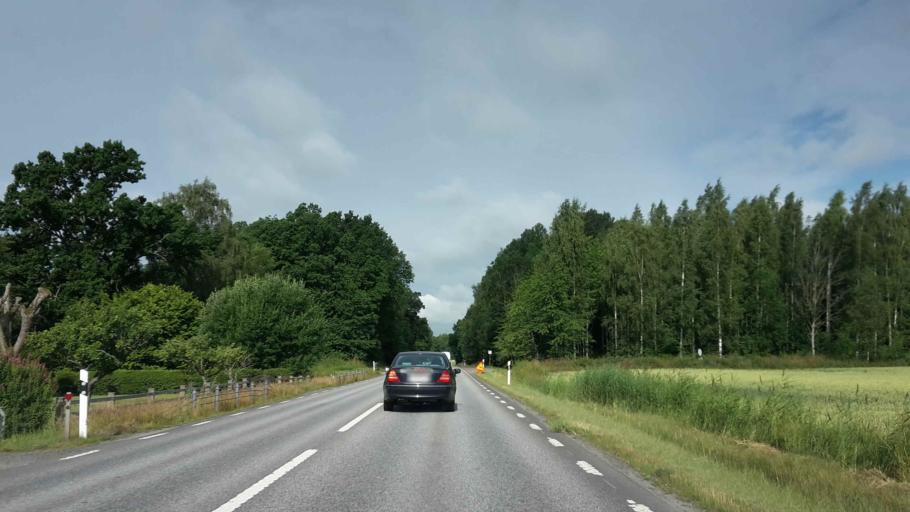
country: SE
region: OEstergoetland
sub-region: Motala Kommun
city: Borensberg
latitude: 58.5819
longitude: 15.1747
